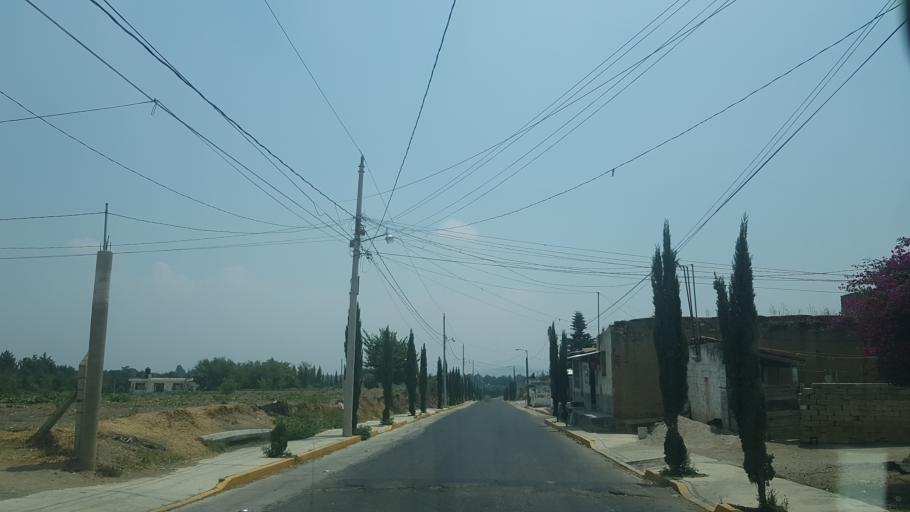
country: MX
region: Puebla
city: San Andres Calpan
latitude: 19.1037
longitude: -98.4496
